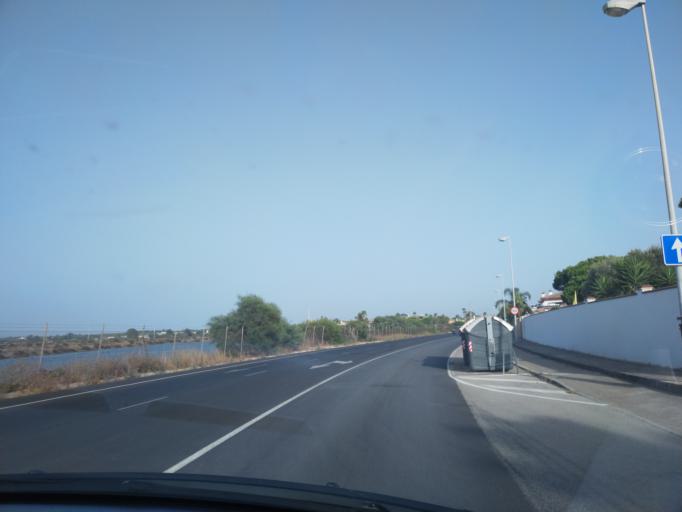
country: ES
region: Andalusia
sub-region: Provincia de Cadiz
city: Chiclana de la Frontera
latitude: 36.3849
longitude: -6.2012
